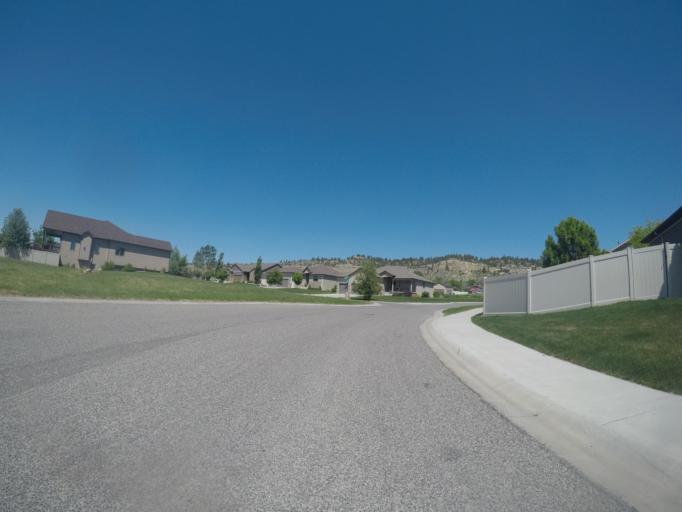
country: US
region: Montana
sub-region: Yellowstone County
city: Billings
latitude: 45.7969
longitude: -108.6100
